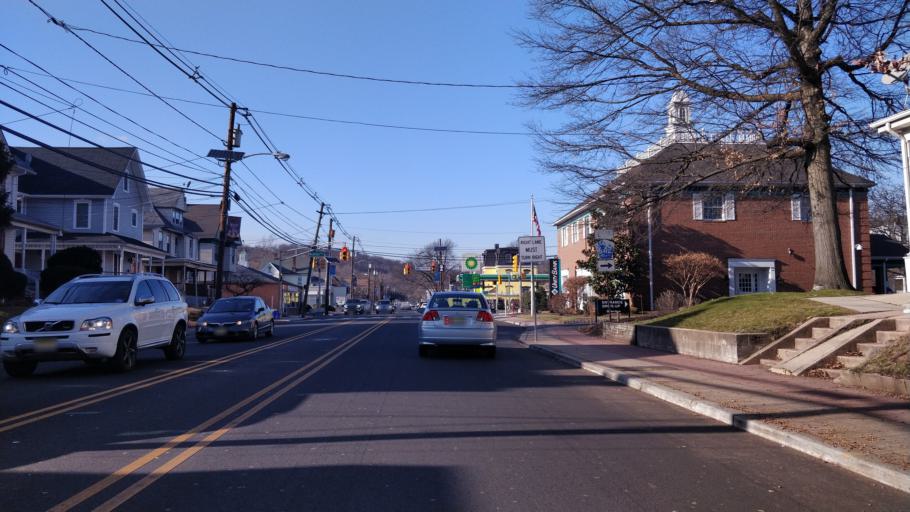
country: US
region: New Jersey
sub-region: Somerset County
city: North Plainfield
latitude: 40.6242
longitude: -74.4333
